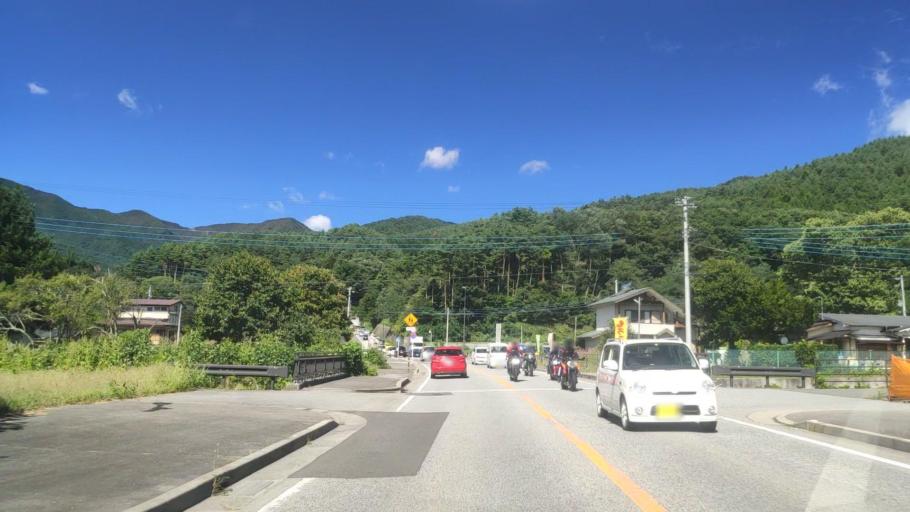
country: JP
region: Yamanashi
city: Fujikawaguchiko
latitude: 35.5238
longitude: 138.7778
